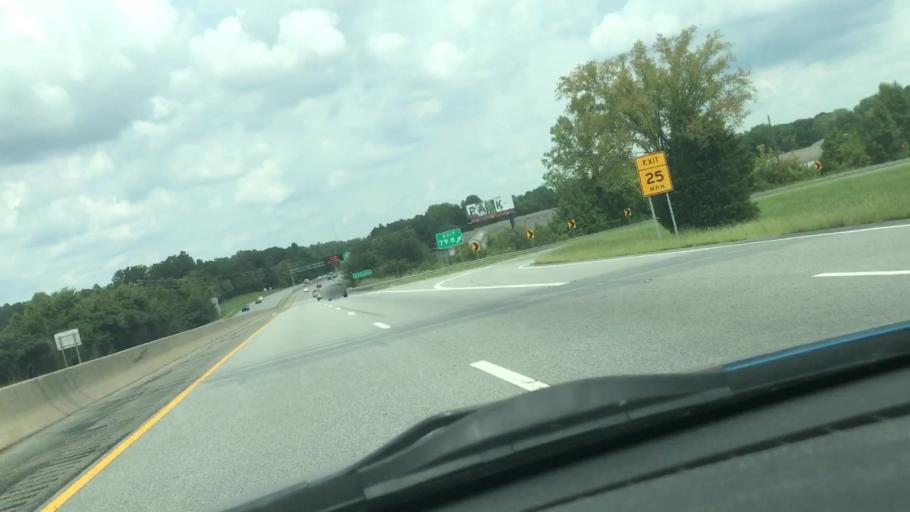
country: US
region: North Carolina
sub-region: Guilford County
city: Greensboro
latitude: 36.0194
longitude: -79.8261
